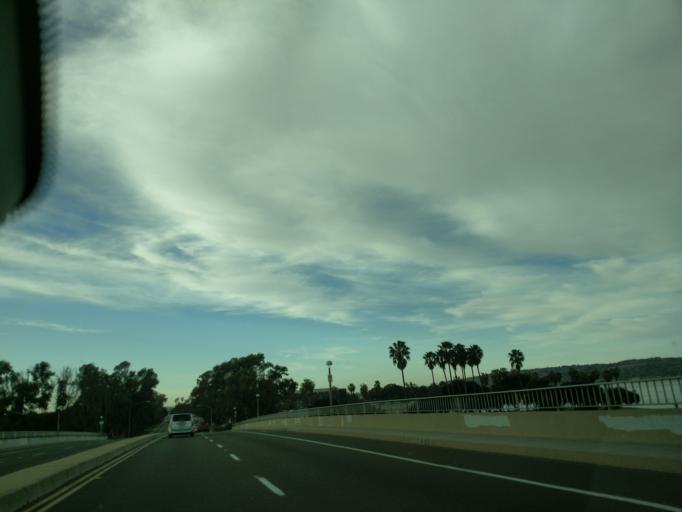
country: US
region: California
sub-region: San Diego County
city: La Jolla
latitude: 32.7682
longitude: -117.2426
